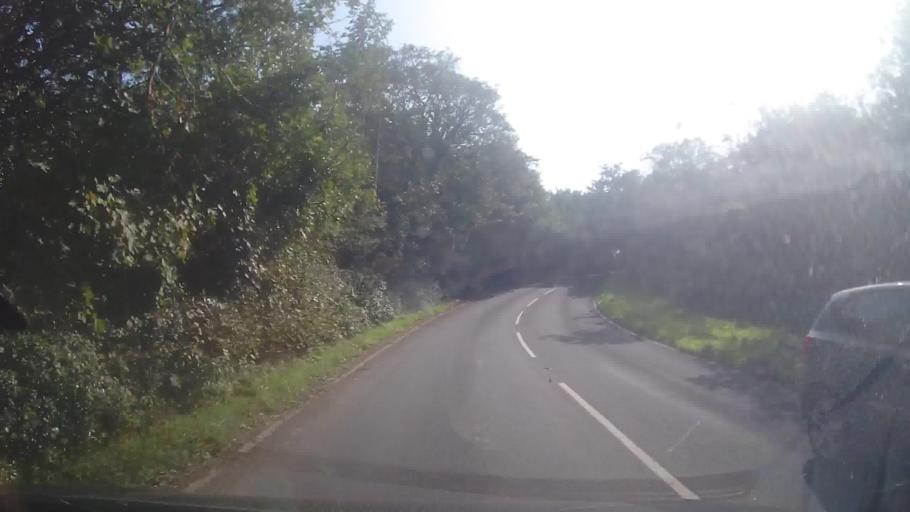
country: GB
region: Wales
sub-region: Pembrokeshire
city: Scleddau
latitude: 51.9806
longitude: -5.0075
